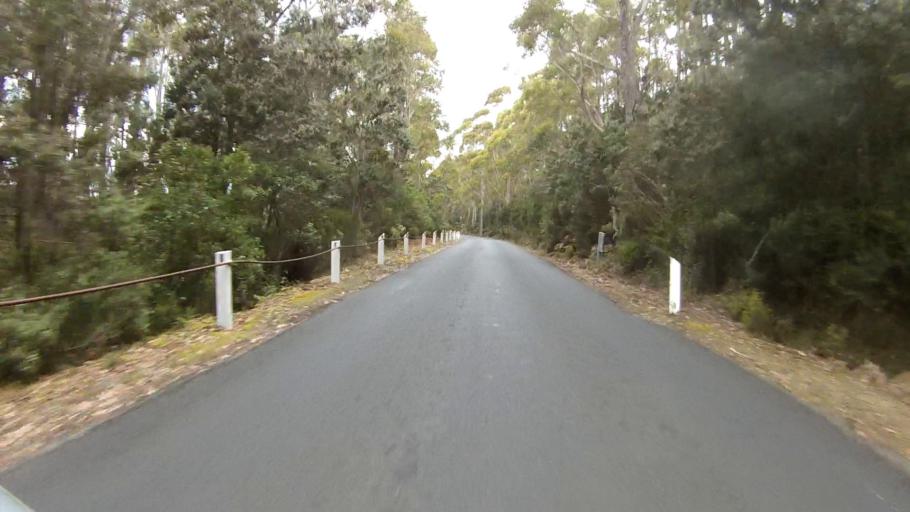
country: AU
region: Tasmania
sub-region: Glenorchy
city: West Moonah
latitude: -42.9036
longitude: 147.2433
